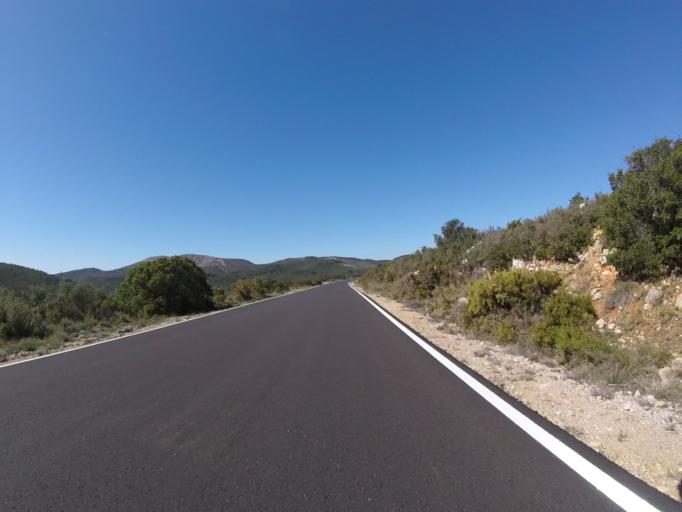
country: ES
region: Valencia
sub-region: Provincia de Castello
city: Cervera del Maestre
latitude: 40.4047
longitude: 0.2131
